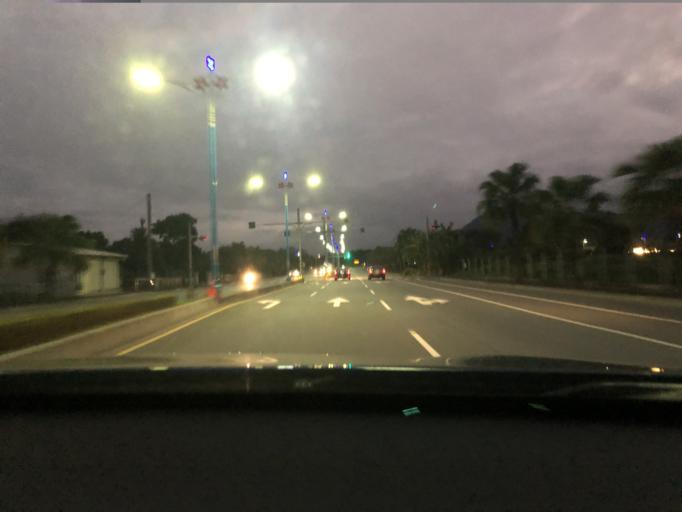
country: TW
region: Taiwan
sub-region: Hualien
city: Hualian
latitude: 23.9549
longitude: 121.5607
